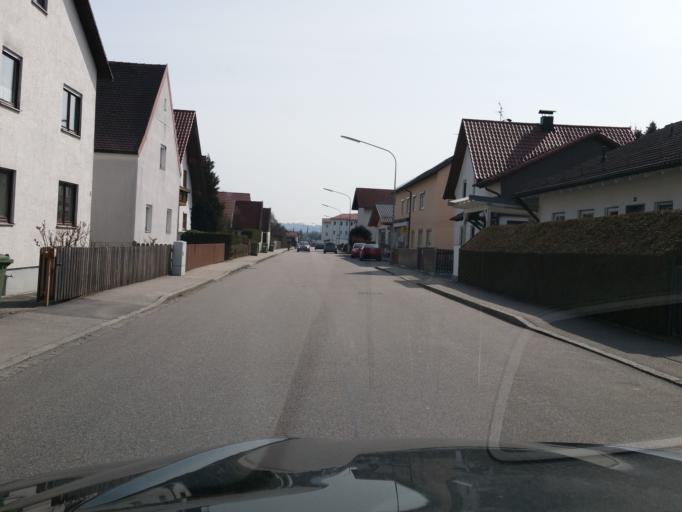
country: DE
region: Bavaria
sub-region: Lower Bavaria
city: Landshut
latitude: 48.5562
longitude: 12.1124
